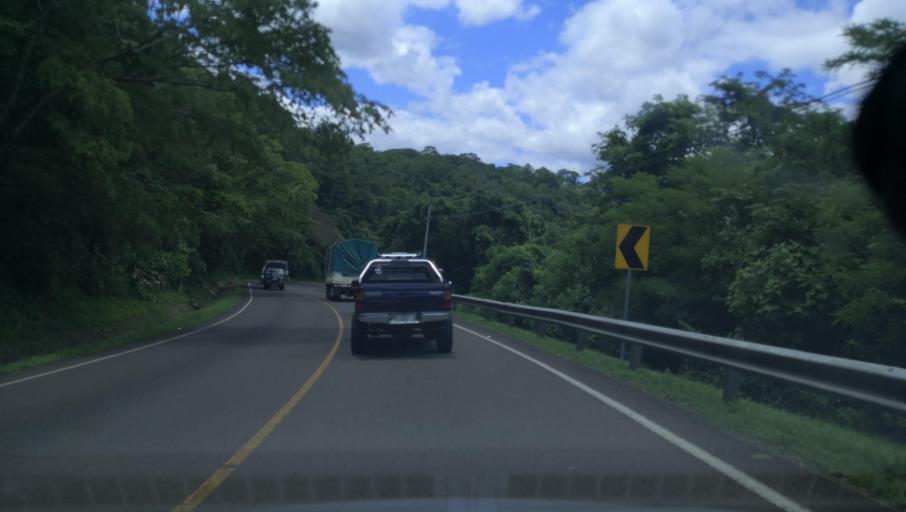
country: NI
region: Esteli
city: Condega
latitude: 13.2514
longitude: -86.3549
